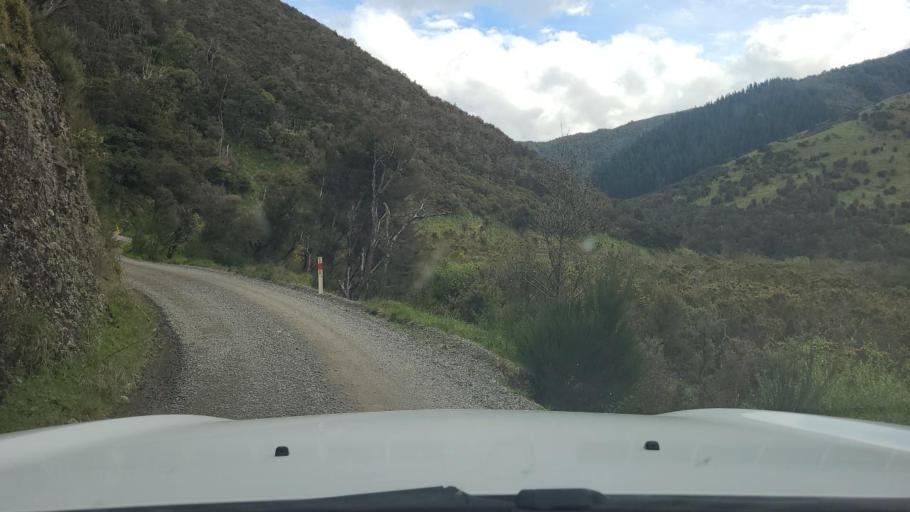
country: NZ
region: Wellington
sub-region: Masterton District
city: Masterton
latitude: -40.9335
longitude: 175.4787
